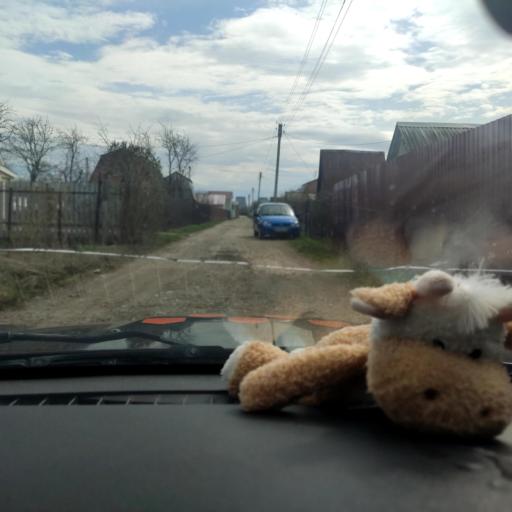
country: RU
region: Samara
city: Tol'yatti
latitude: 53.5984
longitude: 49.2408
